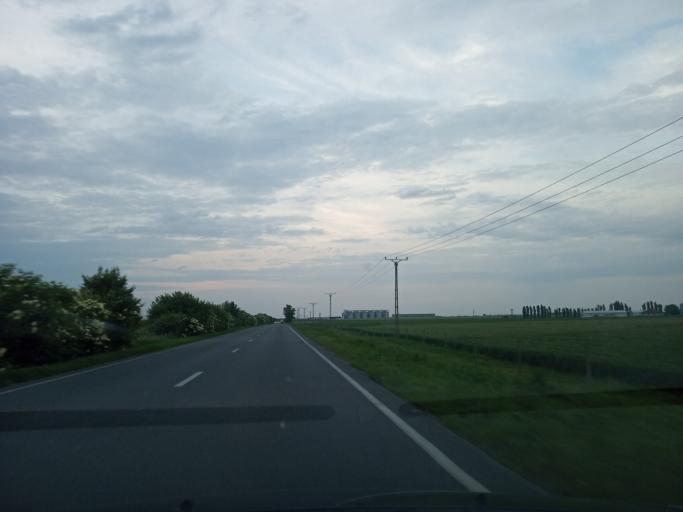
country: RO
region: Timis
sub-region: Comuna Voiteg
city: Voiteg
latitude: 45.4317
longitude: 21.2309
